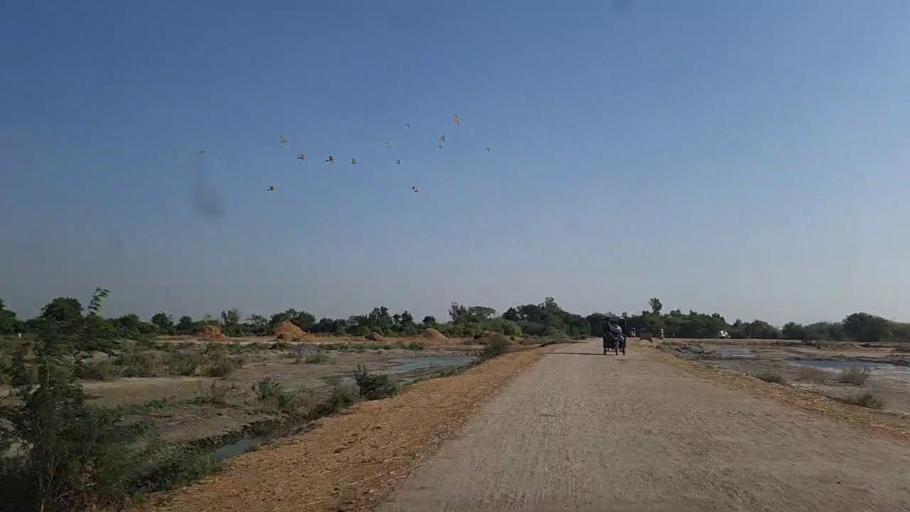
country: PK
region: Sindh
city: Daro Mehar
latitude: 24.6259
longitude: 68.0802
